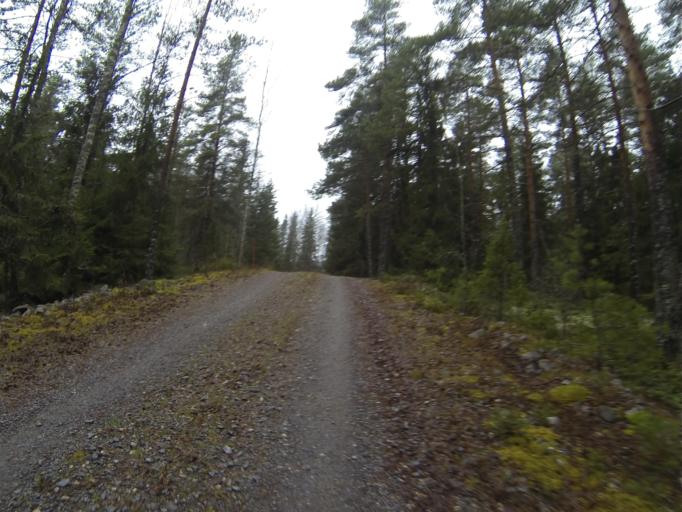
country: FI
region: Varsinais-Suomi
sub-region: Salo
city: Halikko
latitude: 60.4100
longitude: 22.9929
